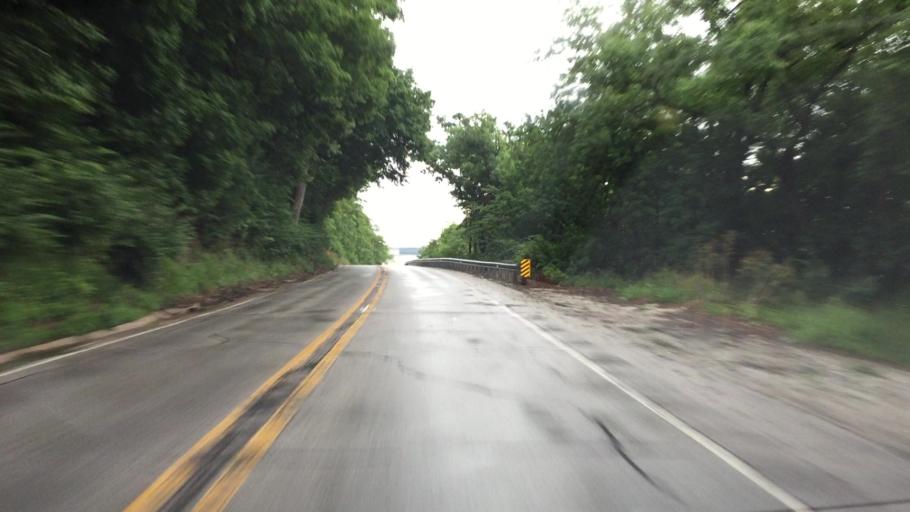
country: US
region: Iowa
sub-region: Lee County
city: Keokuk
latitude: 40.4417
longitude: -91.3717
